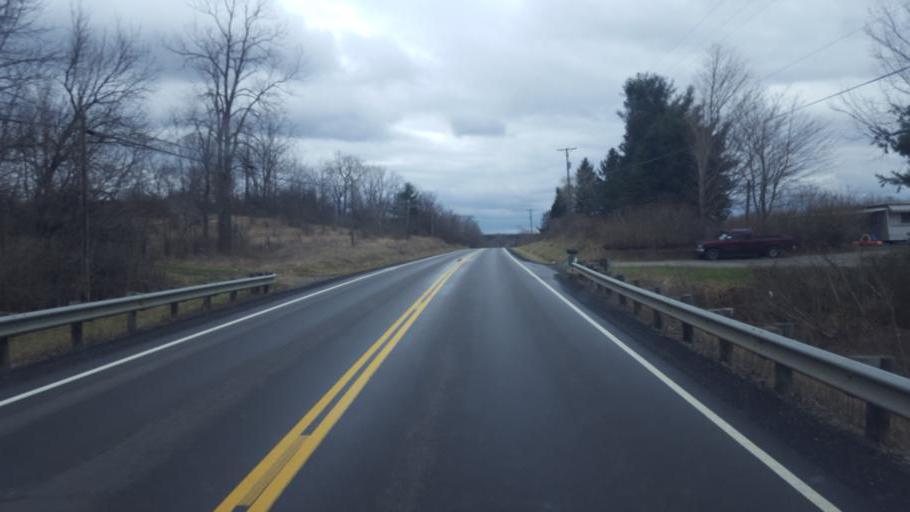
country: US
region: Ohio
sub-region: Knox County
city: Centerburg
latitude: 40.3511
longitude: -82.6152
